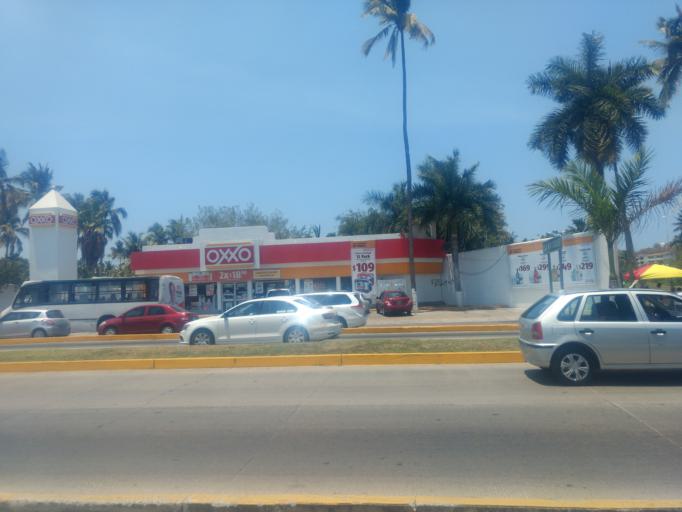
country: MX
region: Colima
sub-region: Manzanillo
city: Manzanillo
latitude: 19.1134
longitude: -104.3424
